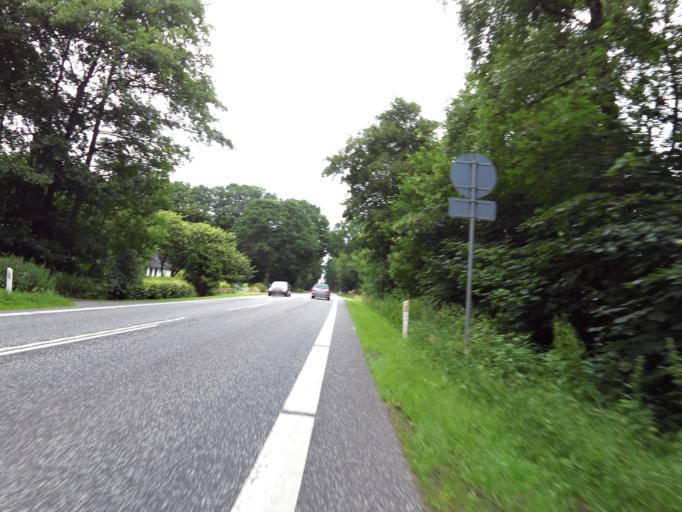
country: DK
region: South Denmark
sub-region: Tonder Kommune
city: Logumkloster
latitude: 55.0942
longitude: 8.9376
